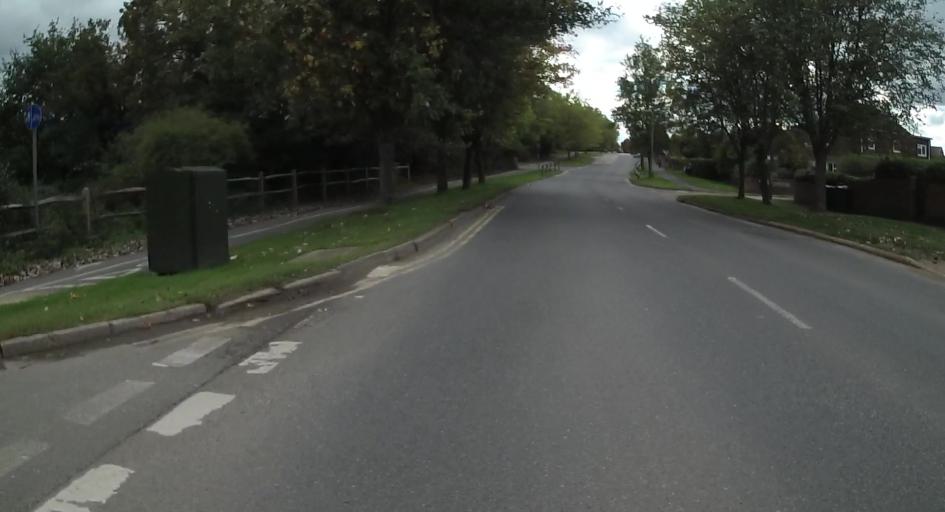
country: GB
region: England
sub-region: Surrey
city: Seale
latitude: 51.2422
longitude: -0.7294
